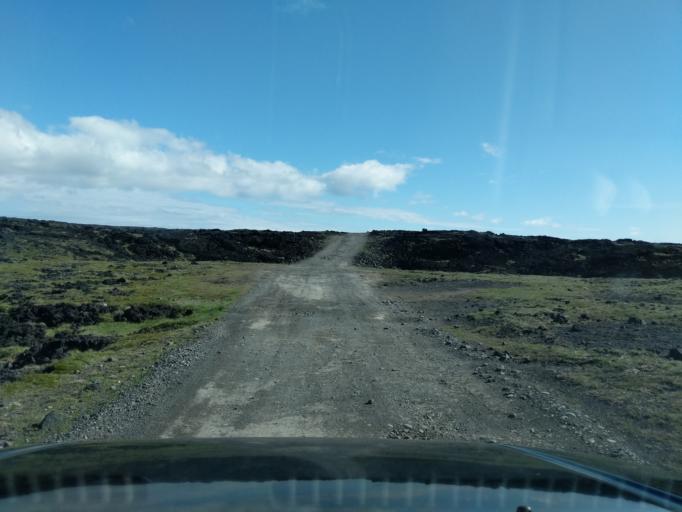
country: IS
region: West
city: Olafsvik
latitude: 64.8697
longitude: -24.0400
